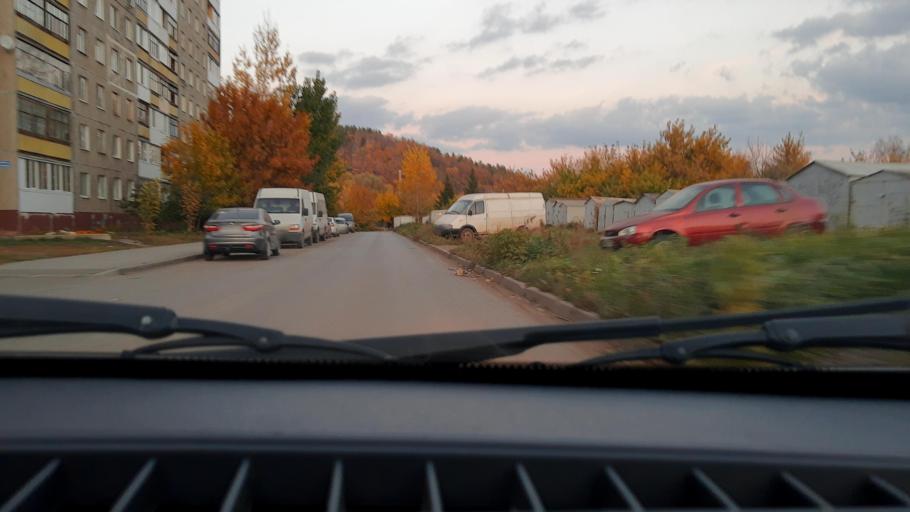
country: RU
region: Bashkortostan
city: Ufa
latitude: 54.8085
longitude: 56.1360
